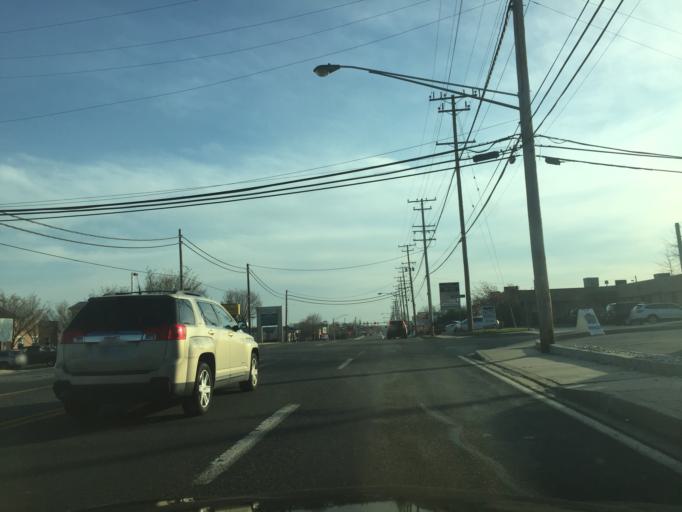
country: US
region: Maryland
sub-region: Baltimore County
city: Perry Hall
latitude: 39.4157
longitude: -76.4606
